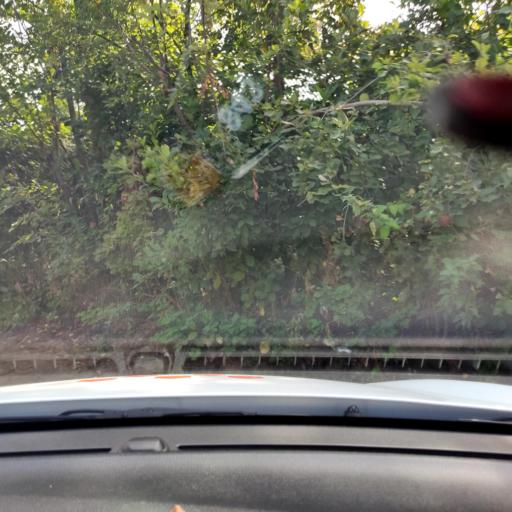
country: RU
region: Tatarstan
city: Staroye Arakchino
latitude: 55.8030
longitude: 48.9938
